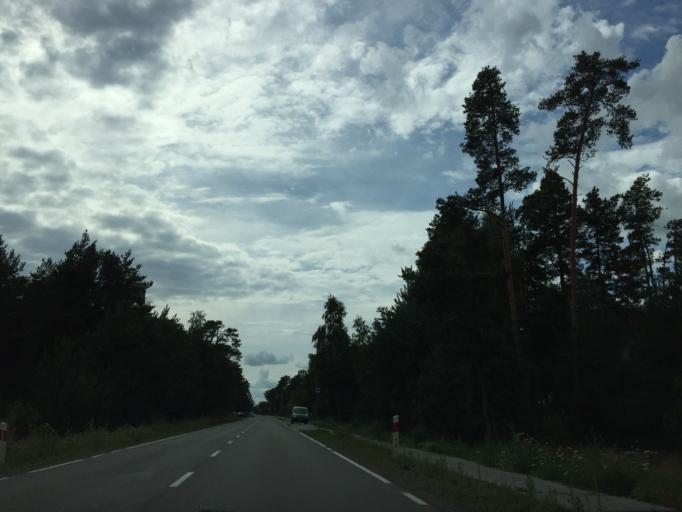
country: PL
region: Lublin Voivodeship
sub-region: Powiat bialski
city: Rzeczyca
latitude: 51.9757
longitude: 22.7099
